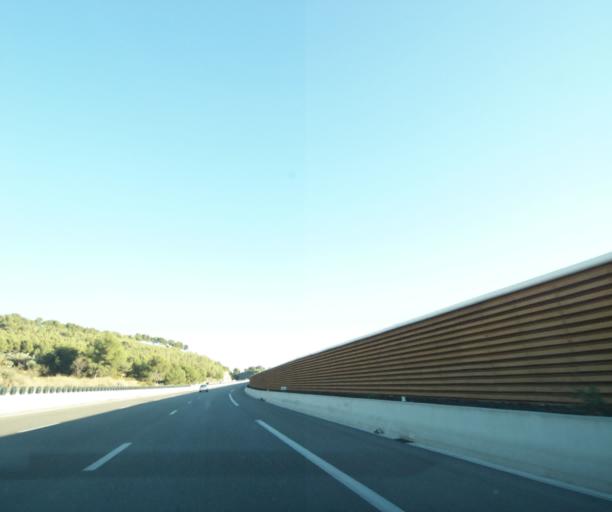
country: FR
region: Provence-Alpes-Cote d'Azur
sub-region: Departement des Bouches-du-Rhone
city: Ceyreste
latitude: 43.1951
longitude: 5.6479
